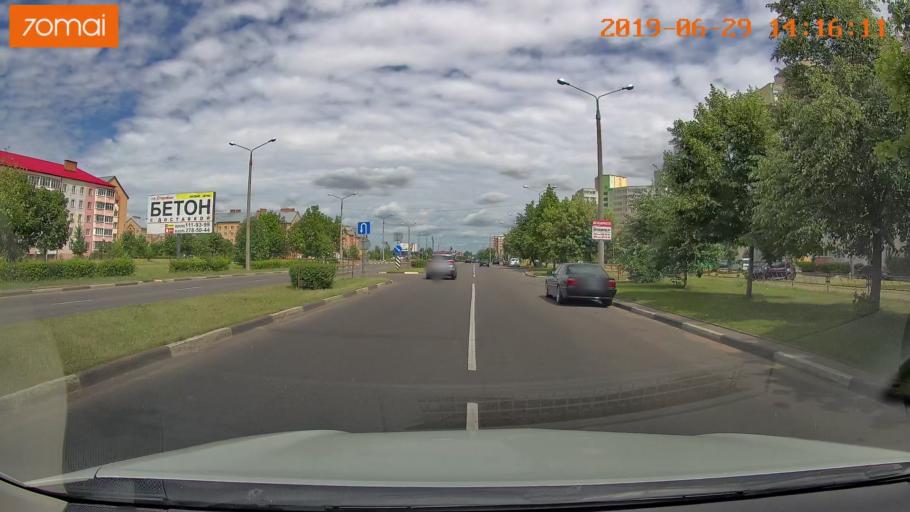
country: BY
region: Minsk
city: Salihorsk
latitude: 52.7945
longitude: 27.5291
